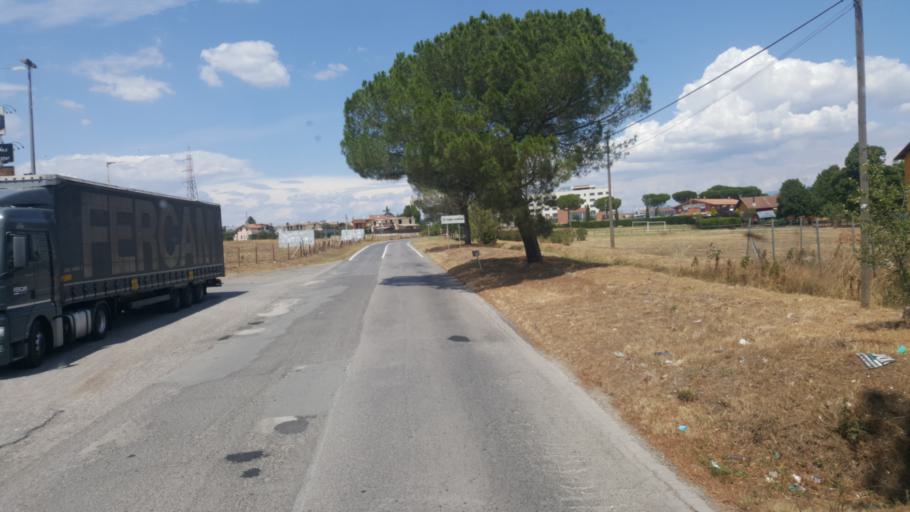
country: IT
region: Latium
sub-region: Citta metropolitana di Roma Capitale
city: Bivio di Capanelle
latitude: 42.1323
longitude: 12.5983
